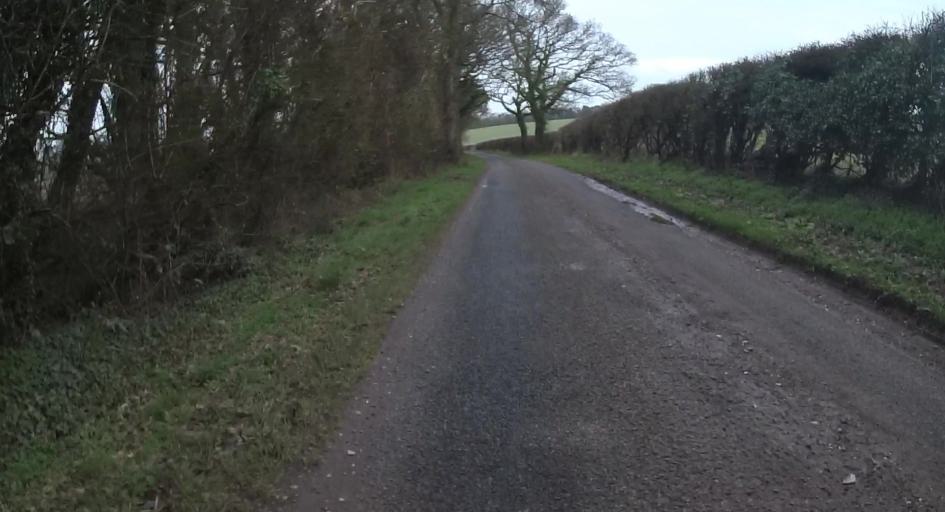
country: GB
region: England
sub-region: Hampshire
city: Overton
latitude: 51.2715
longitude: -1.2515
